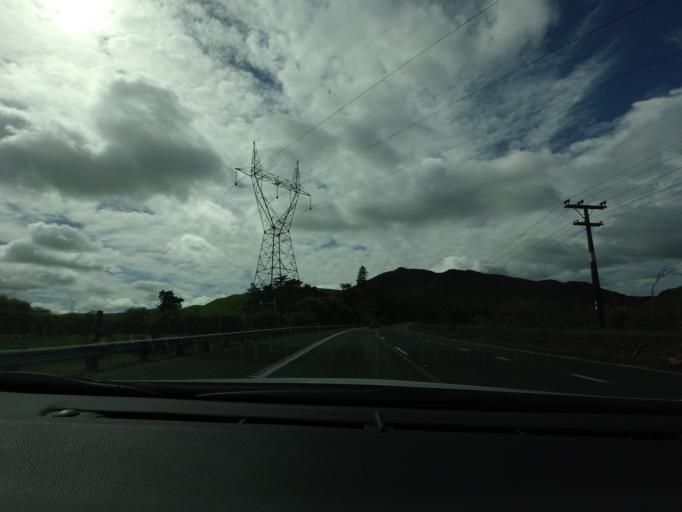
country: NZ
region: Bay of Plenty
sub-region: Rotorua District
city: Rotorua
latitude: -38.3079
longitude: 176.3746
